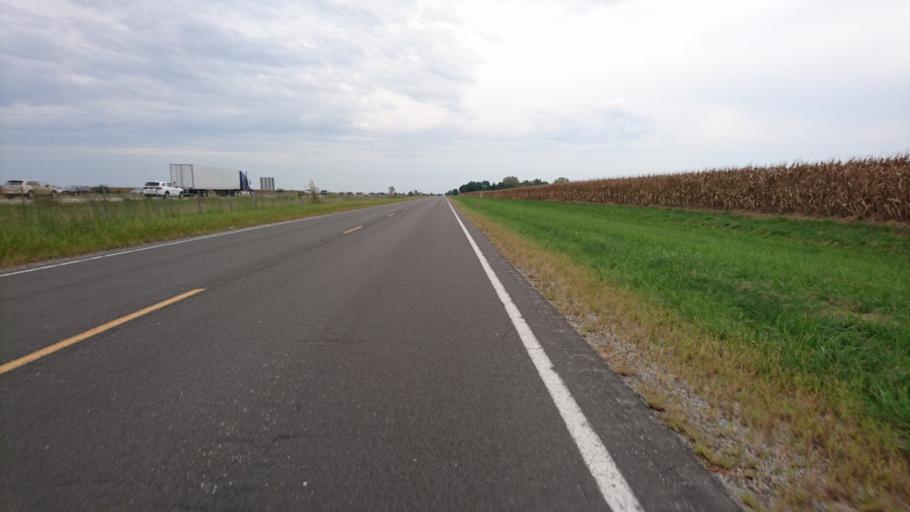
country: US
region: Illinois
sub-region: Sangamon County
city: Chatham
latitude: 39.6650
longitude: -89.6480
